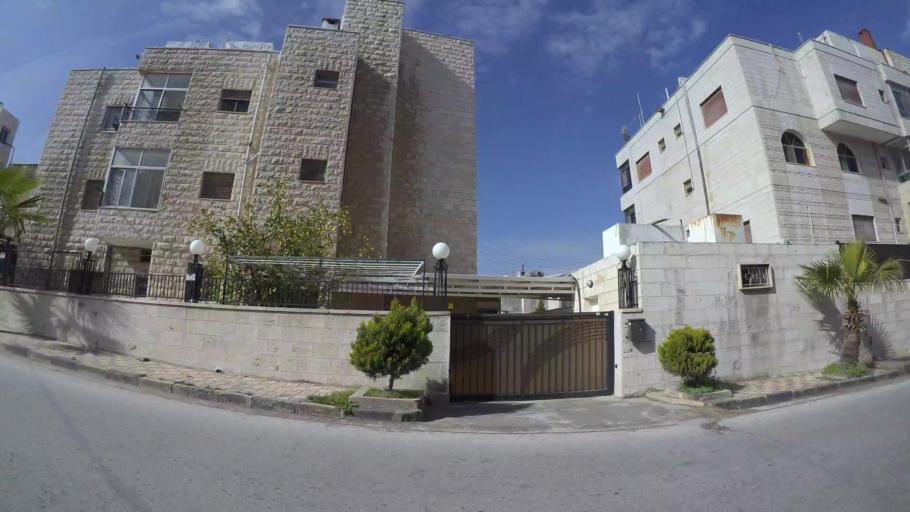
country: JO
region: Amman
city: Al Jubayhah
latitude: 32.0027
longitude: 35.8859
